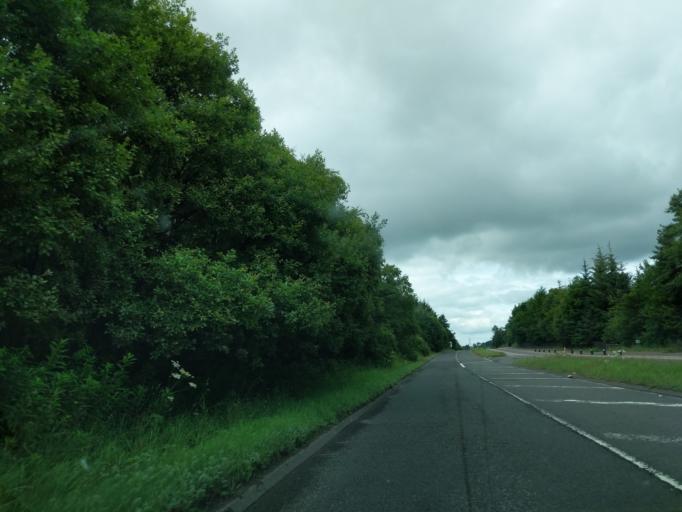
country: GB
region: Scotland
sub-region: South Lanarkshire
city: Douglas
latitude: 55.5876
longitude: -3.8271
